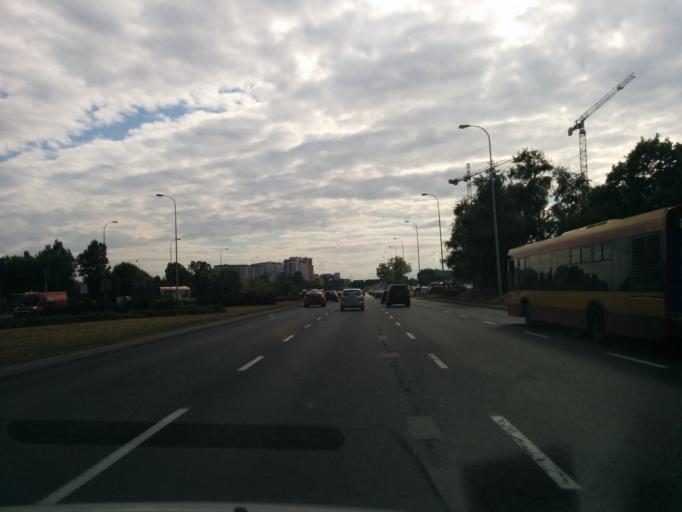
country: PL
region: Masovian Voivodeship
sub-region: Warszawa
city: Ochota
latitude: 52.2197
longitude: 20.9703
